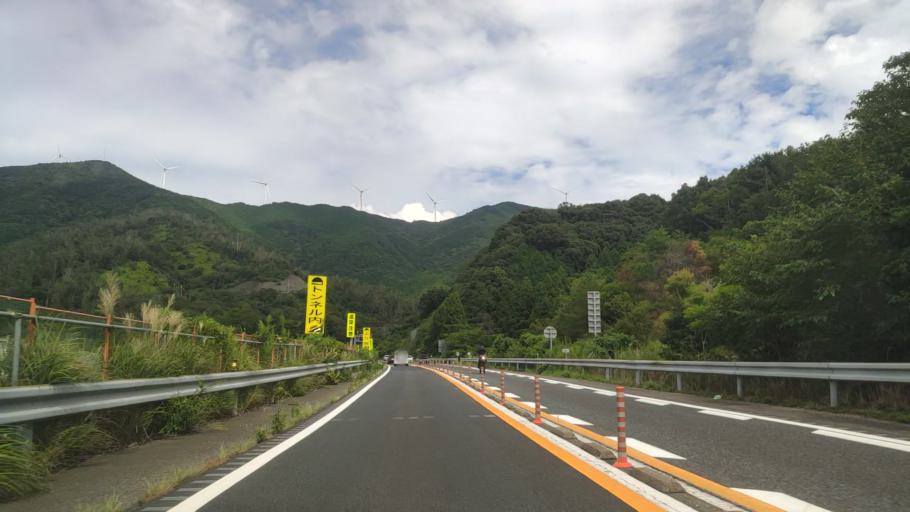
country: JP
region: Wakayama
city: Gobo
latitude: 33.9399
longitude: 135.1976
